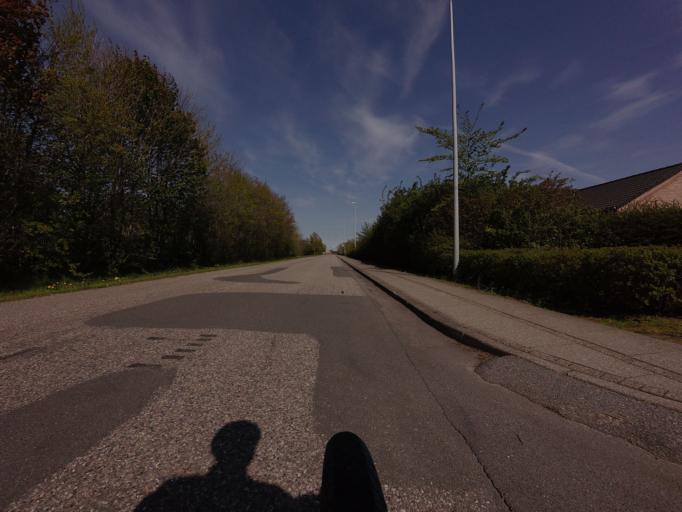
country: DK
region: North Denmark
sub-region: Jammerbugt Kommune
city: Pandrup
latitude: 57.2203
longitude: 9.6614
